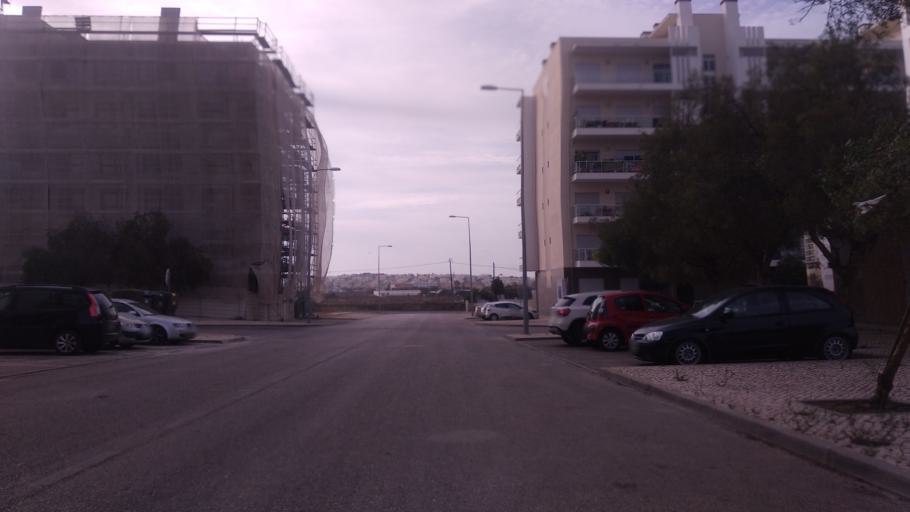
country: PT
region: Faro
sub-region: Faro
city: Faro
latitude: 37.0327
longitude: -7.9385
